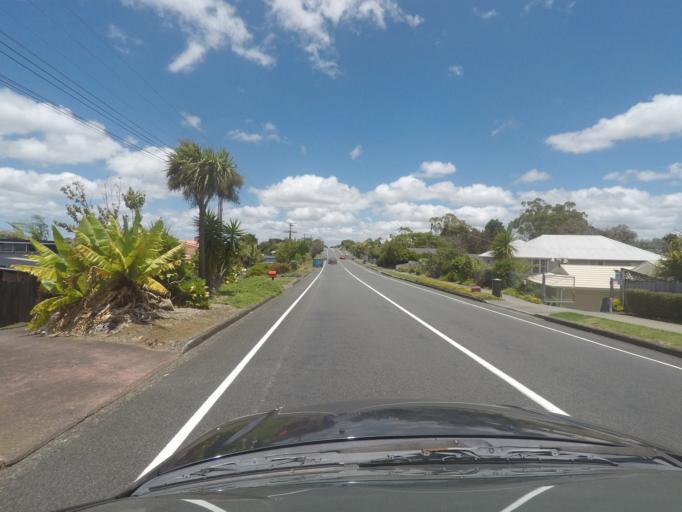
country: NZ
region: Northland
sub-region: Whangarei
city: Whangarei
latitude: -35.7615
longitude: 174.3671
